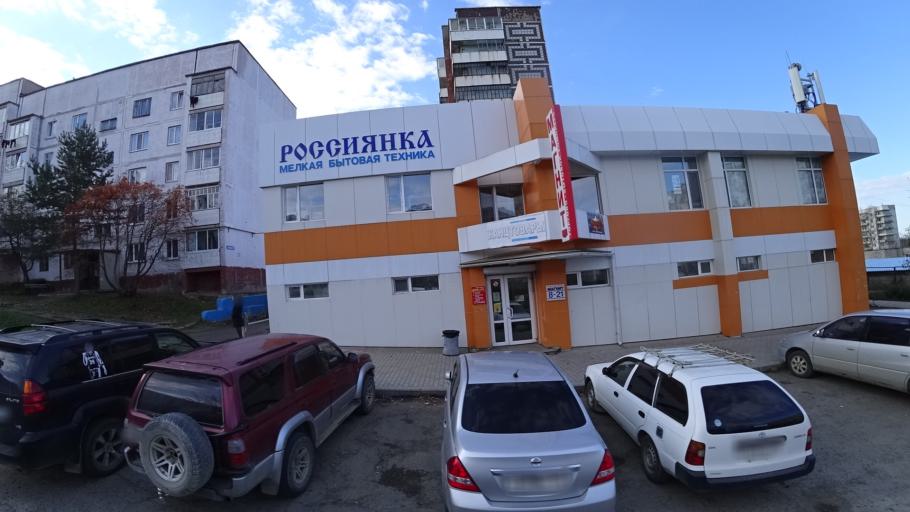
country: RU
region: Khabarovsk Krai
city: Amursk
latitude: 50.2462
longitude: 136.9197
